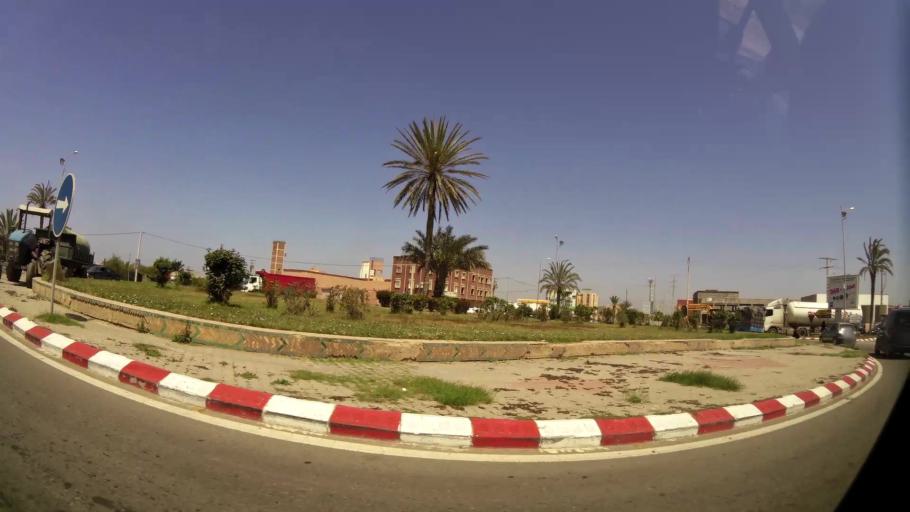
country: MA
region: Souss-Massa-Draa
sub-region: Inezgane-Ait Mellou
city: Inezgane
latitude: 30.3097
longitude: -9.5024
